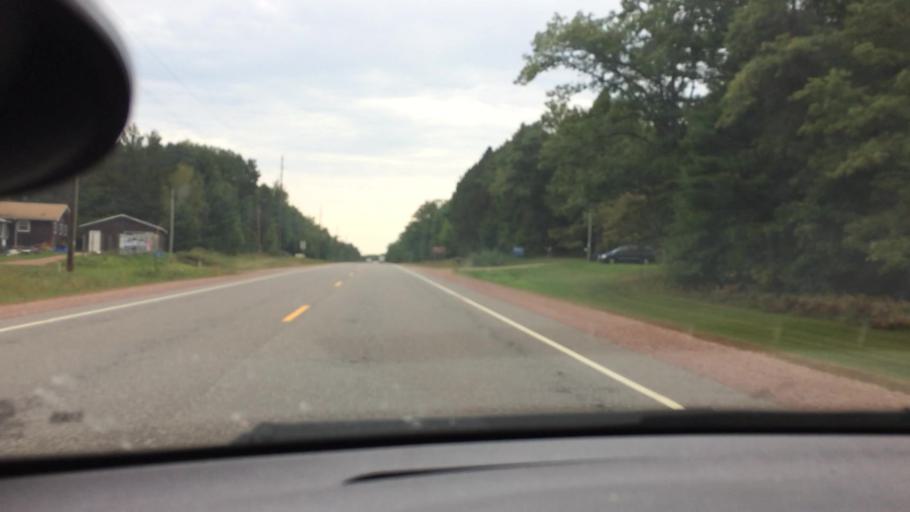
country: US
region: Wisconsin
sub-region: Clark County
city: Neillsville
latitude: 44.5741
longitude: -90.7321
